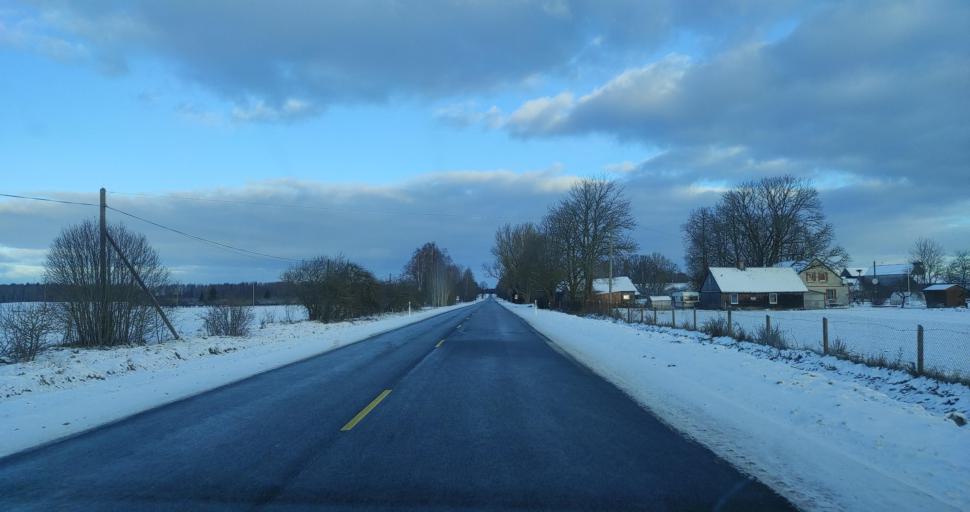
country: LV
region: Skrunda
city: Skrunda
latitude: 56.7075
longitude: 22.0138
